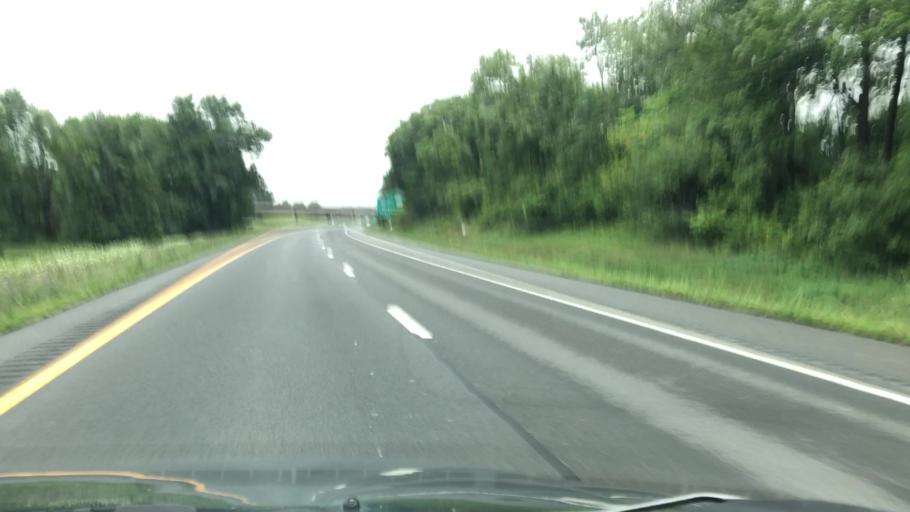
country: US
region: New York
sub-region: Orange County
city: Scotchtown
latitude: 41.4559
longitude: -74.3542
